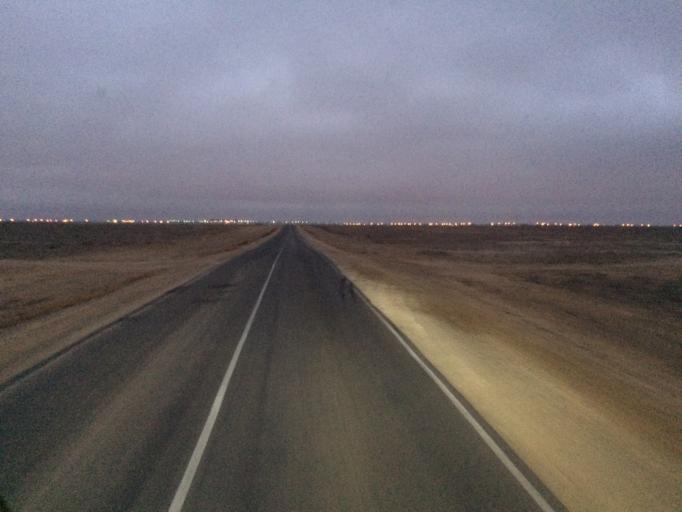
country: KZ
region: Mangghystau
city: Omirzaq
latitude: 43.6172
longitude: 51.3683
